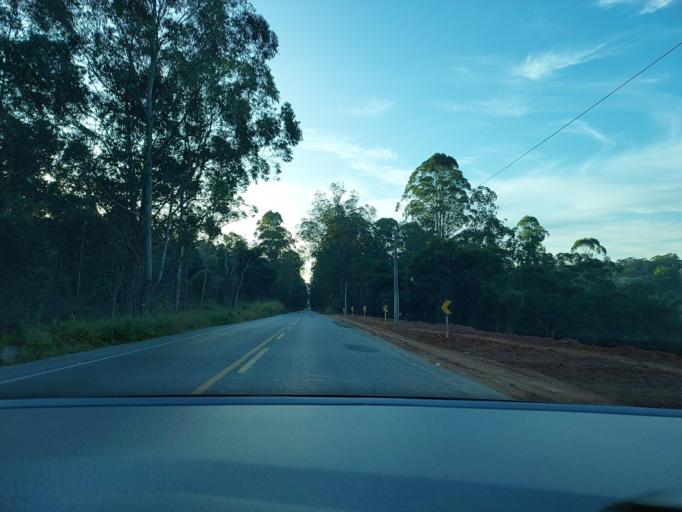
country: BR
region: Minas Gerais
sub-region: Vicosa
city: Vicosa
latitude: -20.8060
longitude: -42.8304
